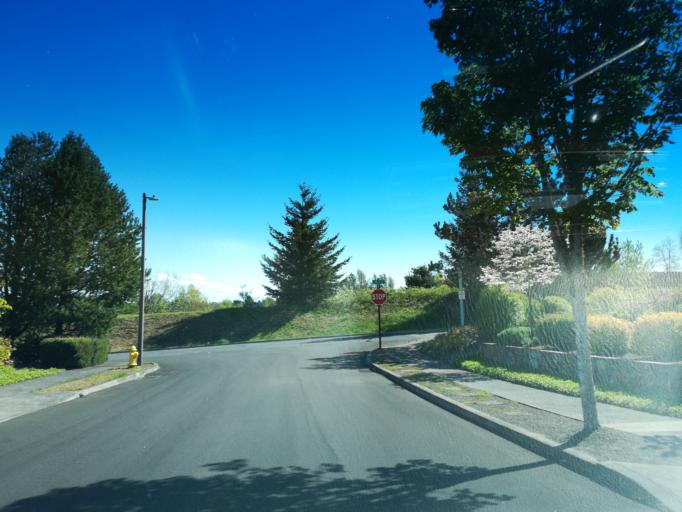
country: US
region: Oregon
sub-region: Multnomah County
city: Troutdale
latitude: 45.5267
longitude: -122.3898
